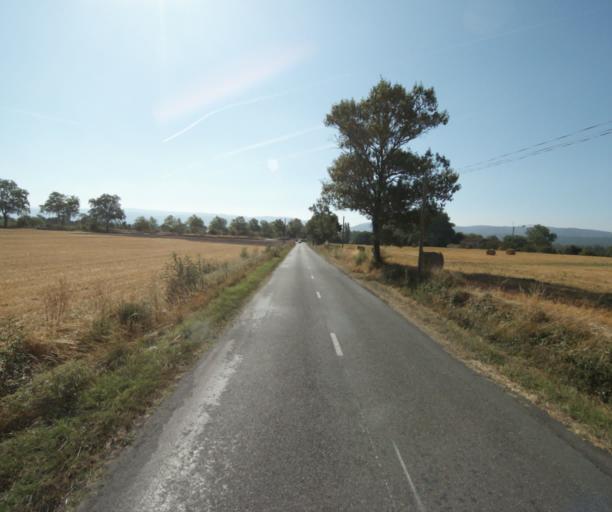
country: FR
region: Midi-Pyrenees
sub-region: Departement de la Haute-Garonne
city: Revel
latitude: 43.4784
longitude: 2.0119
